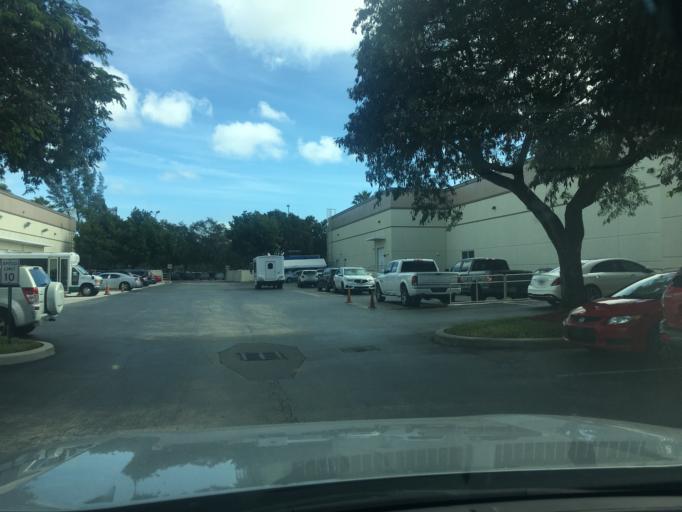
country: US
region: Florida
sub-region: Broward County
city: Dania Beach
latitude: 26.0707
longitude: -80.1799
